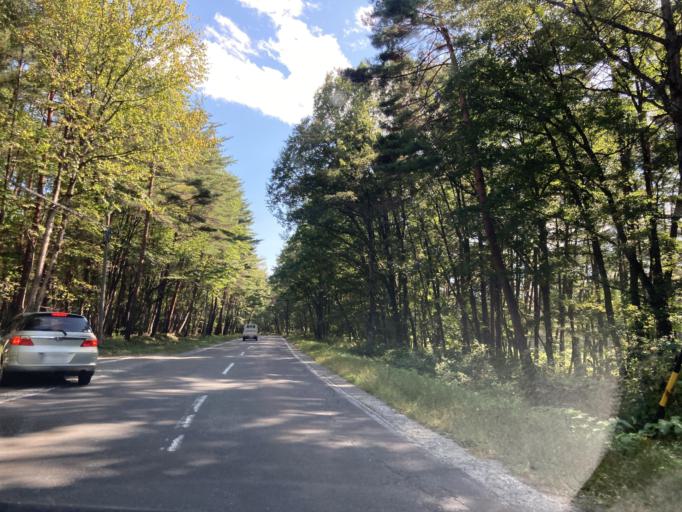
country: JP
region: Nagano
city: Omachi
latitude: 36.5336
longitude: 137.7931
